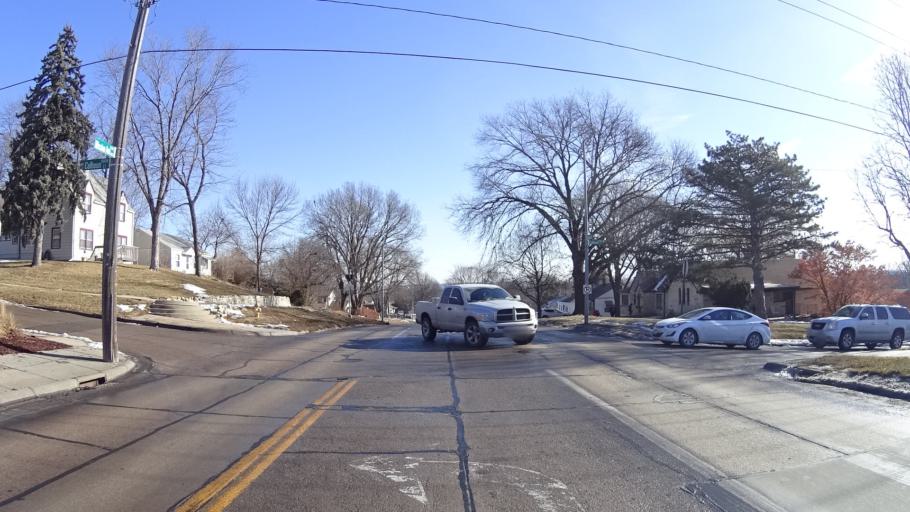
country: US
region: Nebraska
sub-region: Sarpy County
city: Bellevue
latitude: 41.1365
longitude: -95.9045
